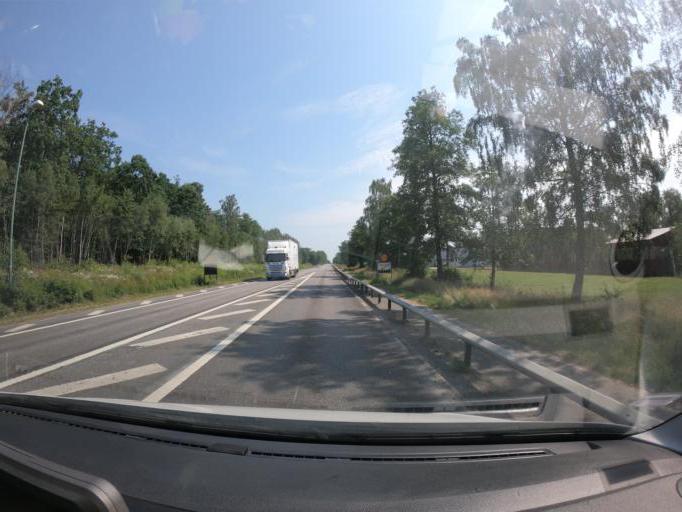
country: SE
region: Skane
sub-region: Hassleholms Kommun
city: Tormestorp
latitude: 56.1630
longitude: 13.6144
